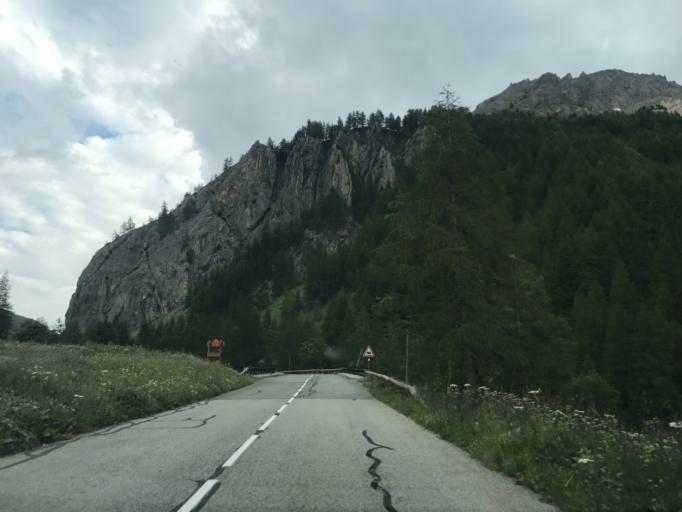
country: FR
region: Rhone-Alpes
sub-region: Departement de la Savoie
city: Valloire
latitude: 45.1199
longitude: 6.4179
